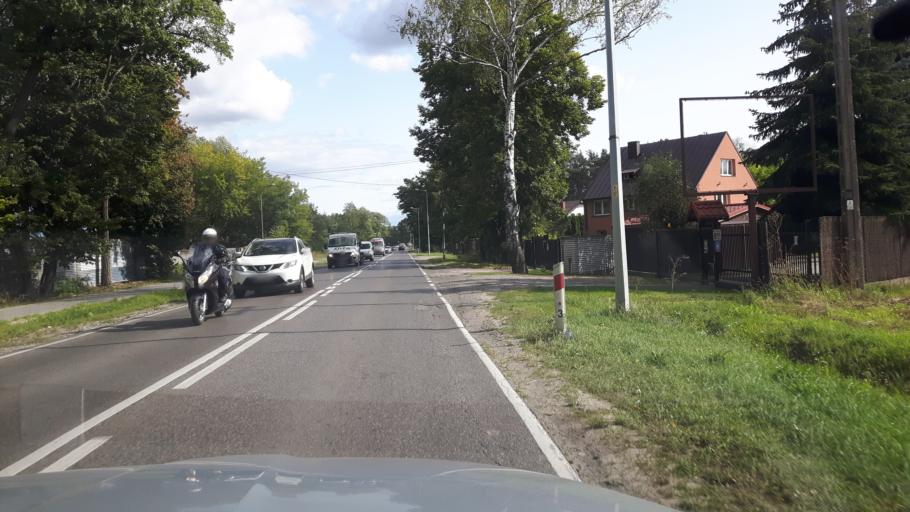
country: PL
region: Masovian Voivodeship
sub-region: Powiat wolominski
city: Wolomin
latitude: 52.3748
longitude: 21.2195
